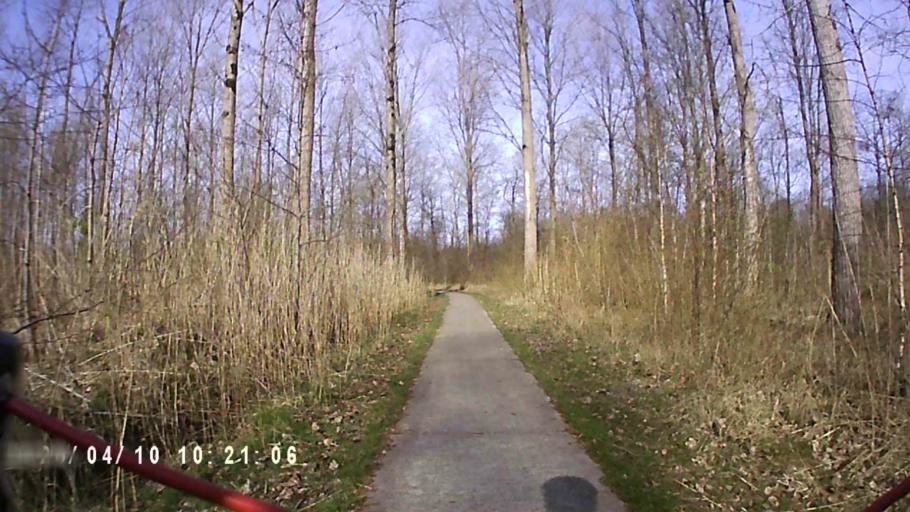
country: NL
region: Friesland
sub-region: Gemeente Dongeradeel
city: Anjum
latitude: 53.3806
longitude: 6.2195
